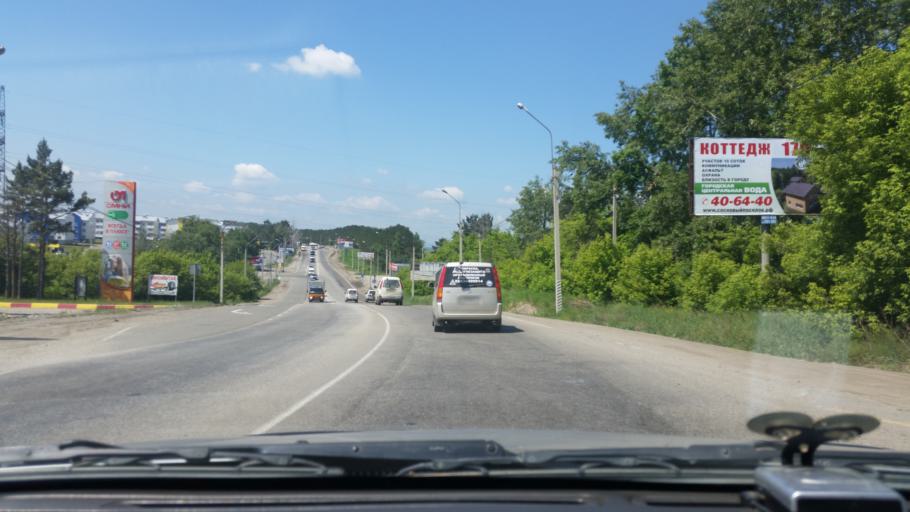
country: RU
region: Irkutsk
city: Smolenshchina
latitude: 52.2614
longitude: 104.1935
